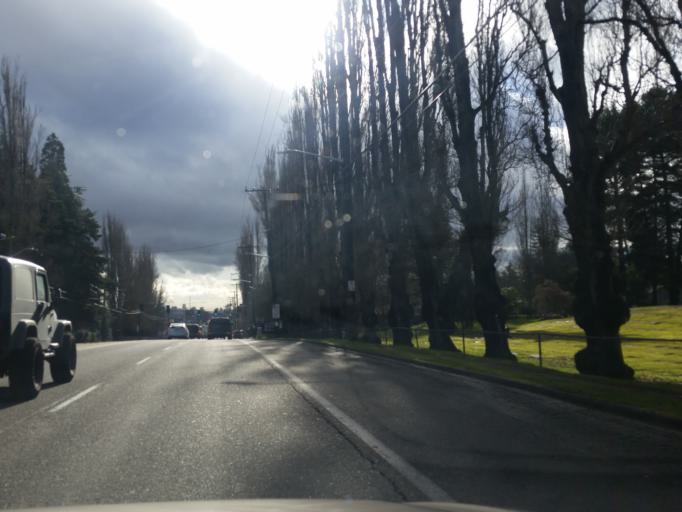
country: US
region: Washington
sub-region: King County
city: Shoreline
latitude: 47.7114
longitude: -122.3449
